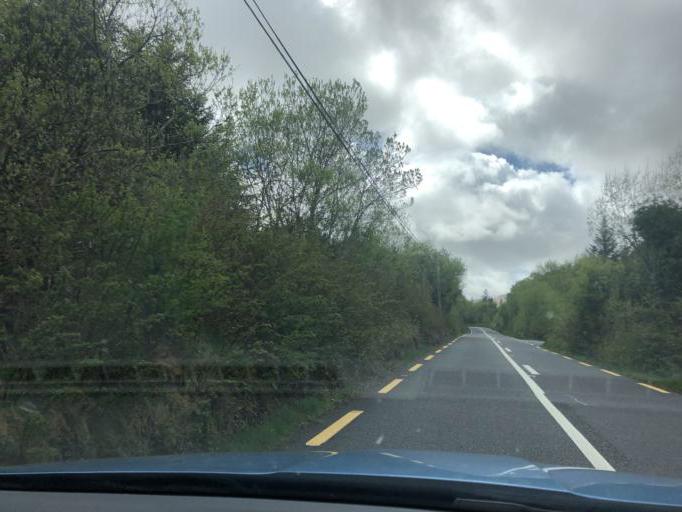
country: IE
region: Munster
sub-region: Ciarrai
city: Cahersiveen
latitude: 51.8273
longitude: -9.9614
